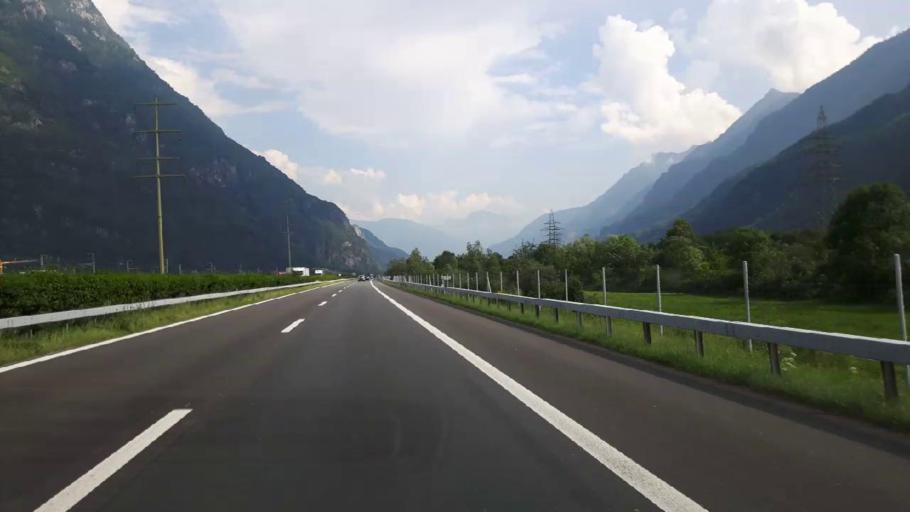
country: CH
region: Ticino
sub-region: Riviera District
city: Biasca
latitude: 46.3460
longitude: 8.9659
